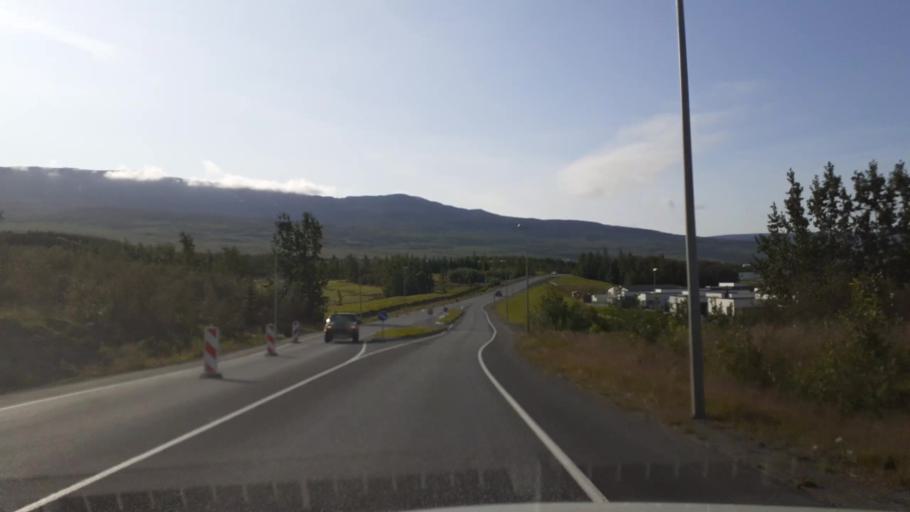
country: IS
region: Northeast
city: Akureyri
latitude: 65.6715
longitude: -18.1173
